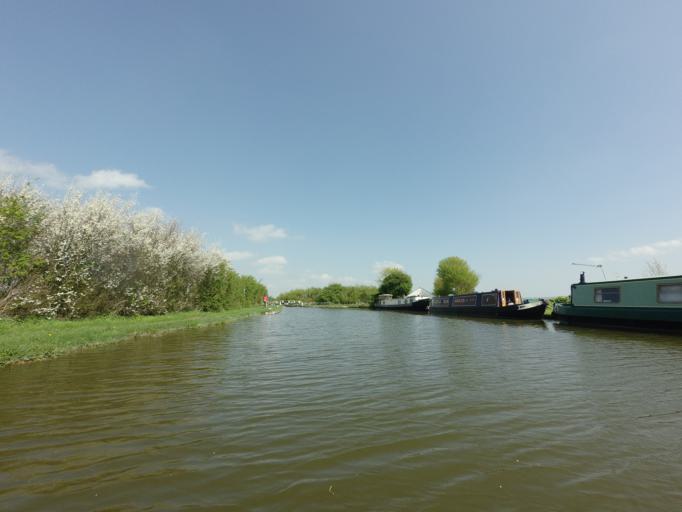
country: GB
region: England
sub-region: Buckinghamshire
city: Ivinghoe
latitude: 51.8452
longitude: -0.6446
